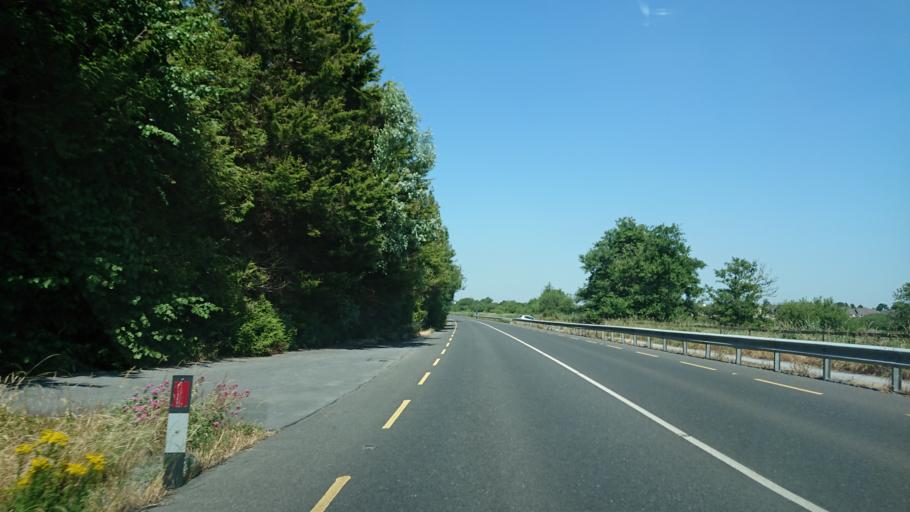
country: IE
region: Munster
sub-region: Waterford
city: Waterford
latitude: 52.2308
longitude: -7.1220
